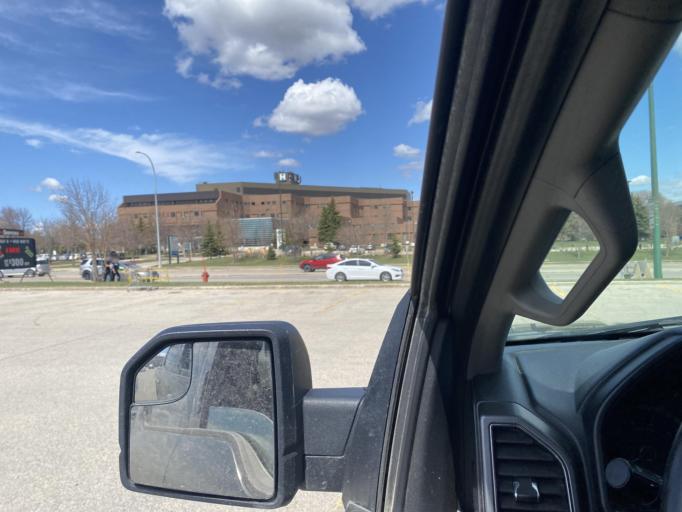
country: CA
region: Manitoba
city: Winnipeg
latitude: 49.9538
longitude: -97.1497
